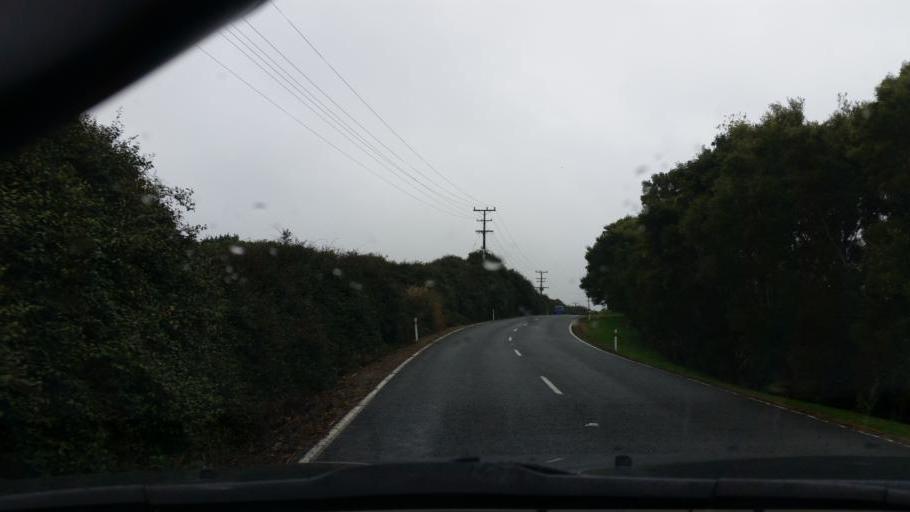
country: NZ
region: Auckland
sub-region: Auckland
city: Wellsford
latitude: -36.1125
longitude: 174.5391
